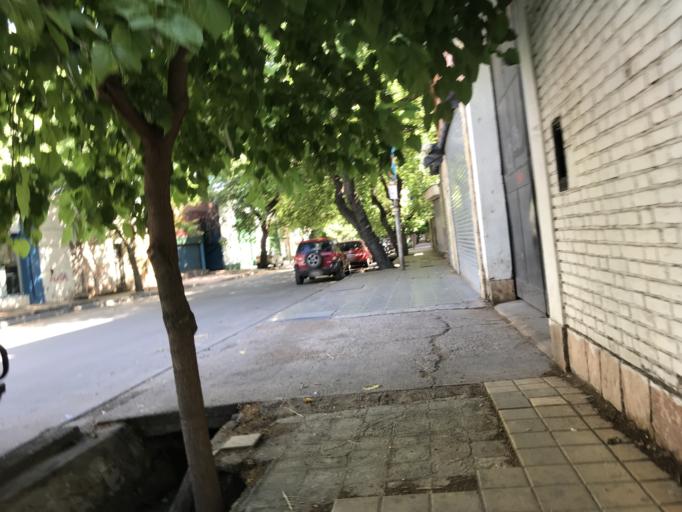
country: AR
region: Mendoza
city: Mendoza
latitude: -32.8813
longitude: -68.8310
